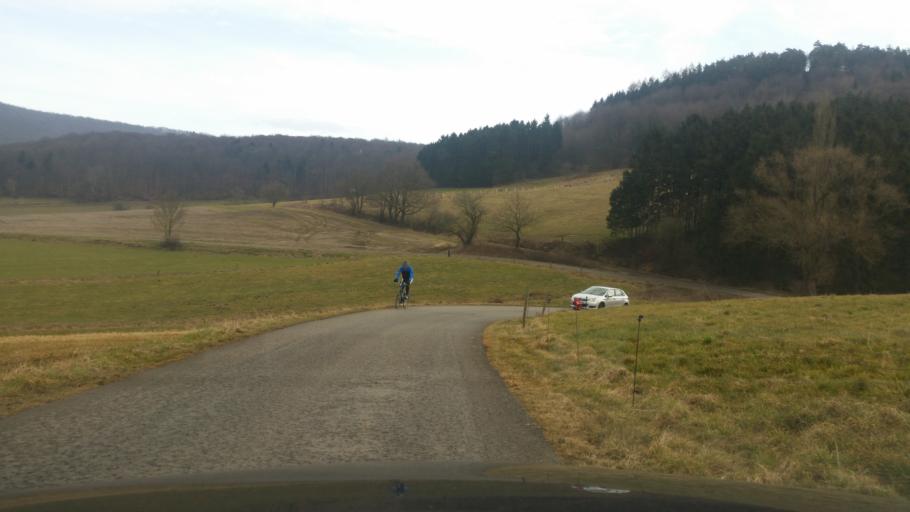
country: DE
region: Lower Saxony
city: Hessisch Oldendorf
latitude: 52.1829
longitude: 9.3136
